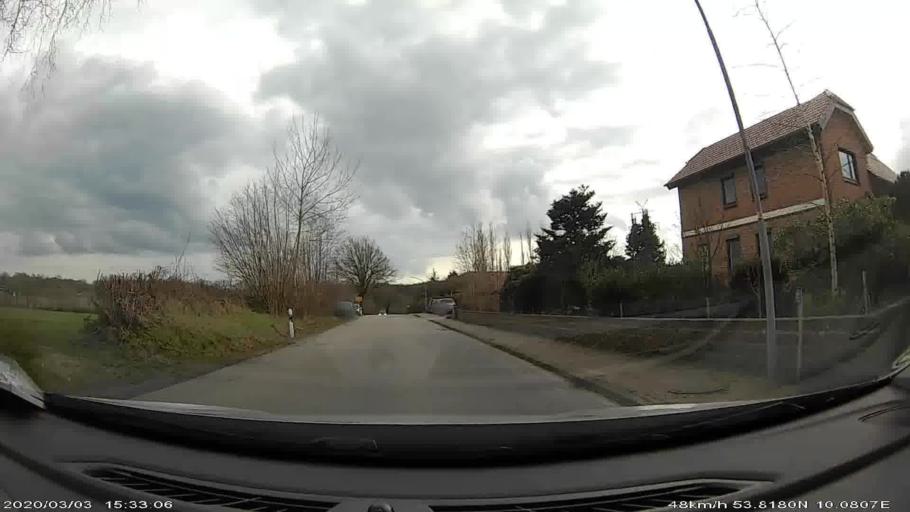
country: DE
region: Schleswig-Holstein
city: Huttblek
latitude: 53.8186
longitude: 10.0808
